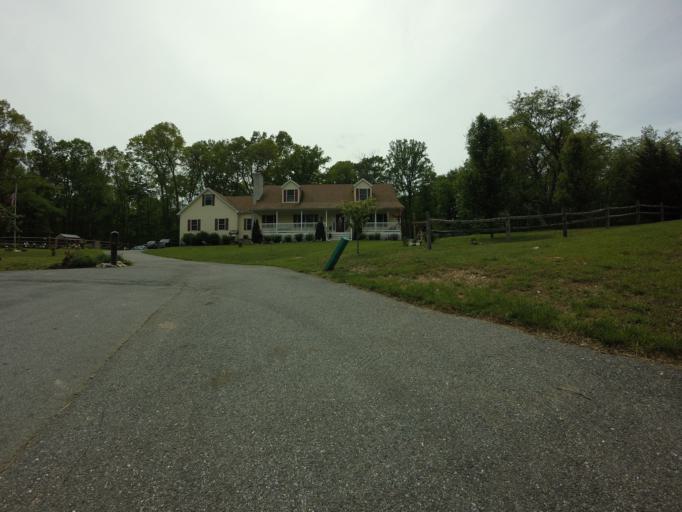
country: US
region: Maryland
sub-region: Carroll County
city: Eldersburg
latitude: 39.4635
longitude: -76.9604
